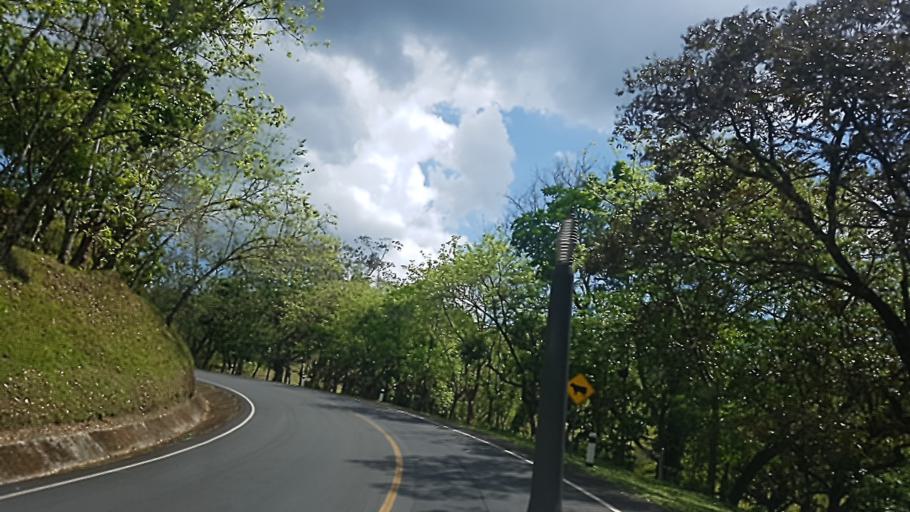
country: NI
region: Atlantico Sur
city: Muelle de los Bueyes
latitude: 11.9831
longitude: -84.7582
